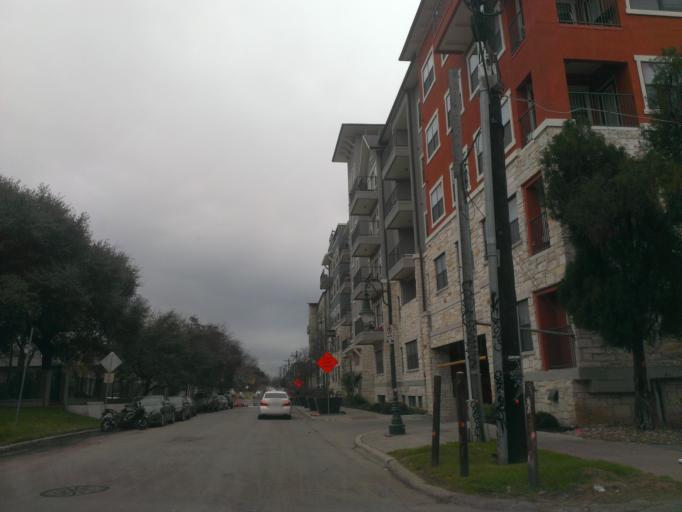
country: US
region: Texas
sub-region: Travis County
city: Austin
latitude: 30.2909
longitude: -97.7492
